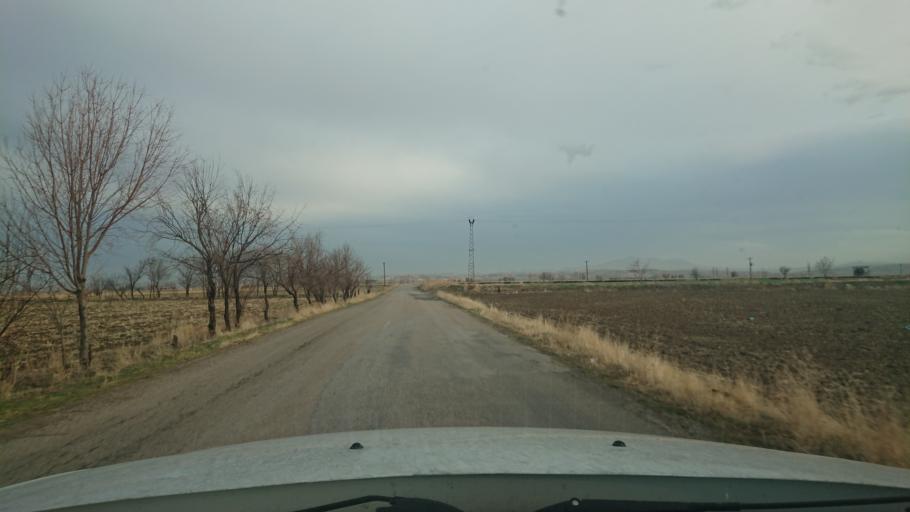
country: TR
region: Aksaray
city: Yesilova
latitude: 38.4311
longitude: 33.8360
